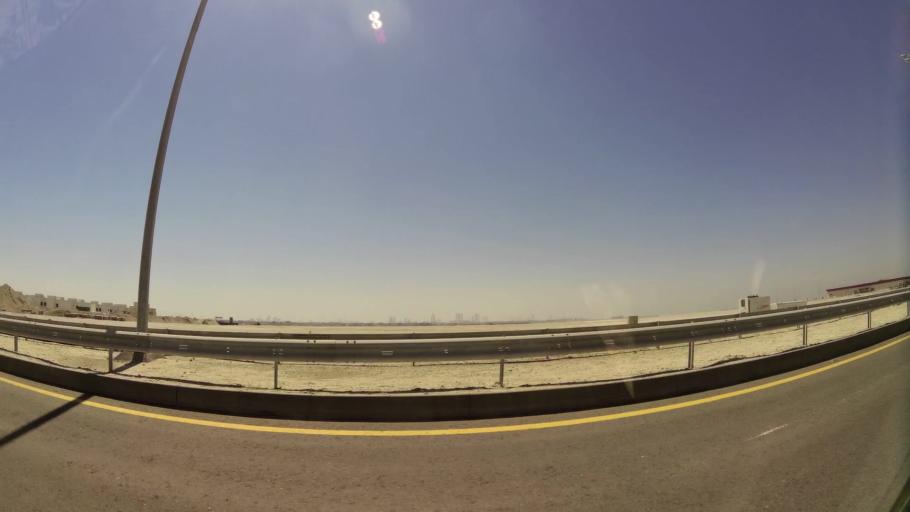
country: BH
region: Muharraq
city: Al Muharraq
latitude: 26.3047
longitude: 50.6309
